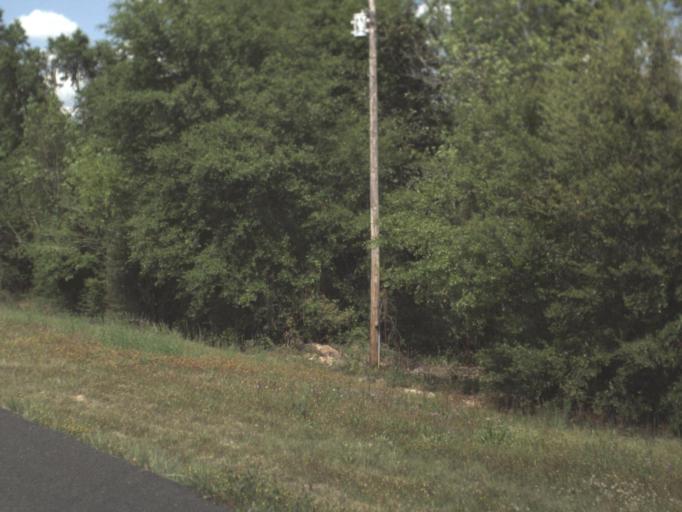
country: US
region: Florida
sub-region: Escambia County
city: Century
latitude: 30.8878
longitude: -87.3211
